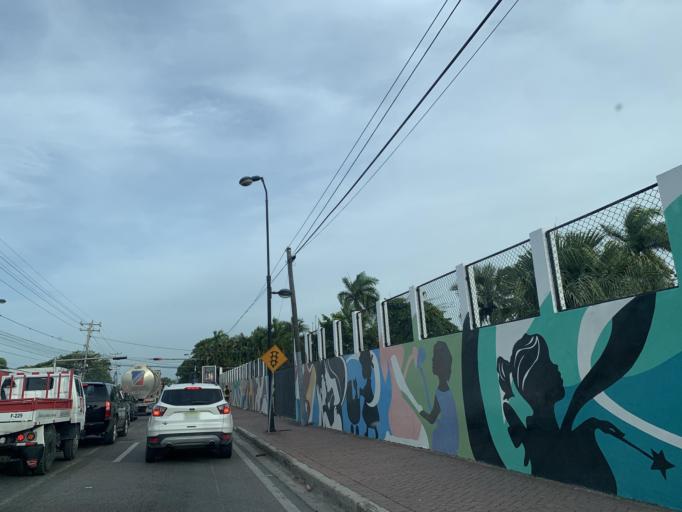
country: DO
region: Puerto Plata
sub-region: Puerto Plata
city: Puerto Plata
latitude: 19.7801
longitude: -70.6707
